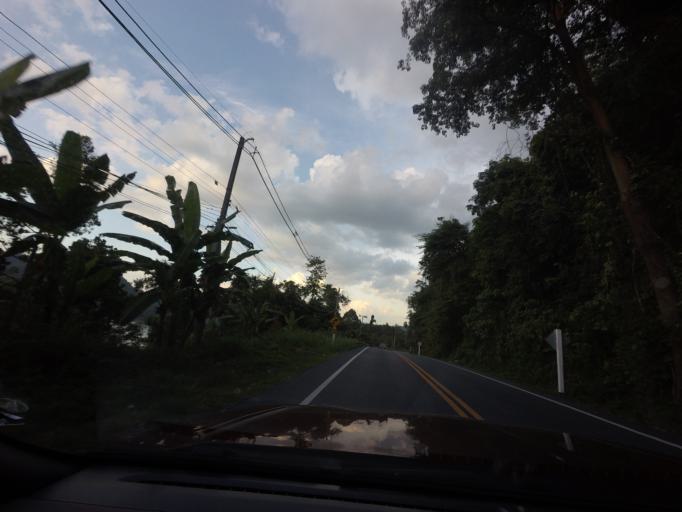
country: TH
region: Yala
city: Than To
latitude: 6.0376
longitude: 101.2017
